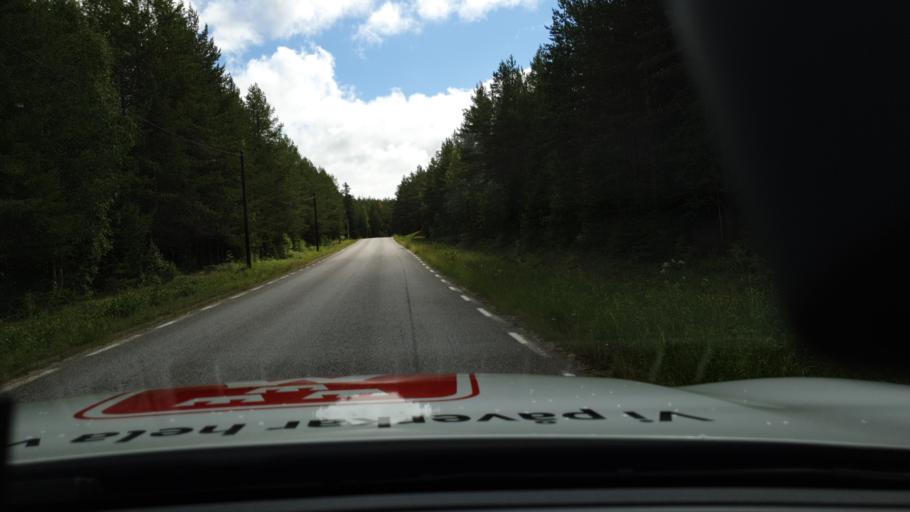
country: SE
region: Norrbotten
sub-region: Lulea Kommun
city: Sodra Sunderbyn
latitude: 65.4639
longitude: 21.9143
